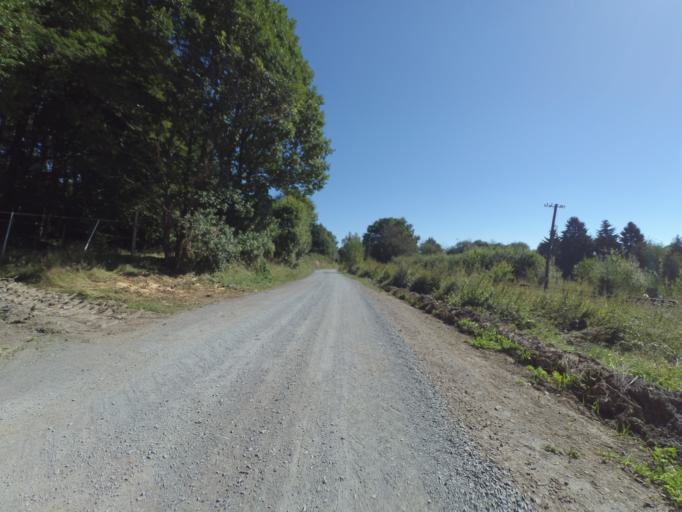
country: DE
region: Rheinland-Pfalz
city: Darscheid
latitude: 50.2109
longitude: 6.8785
